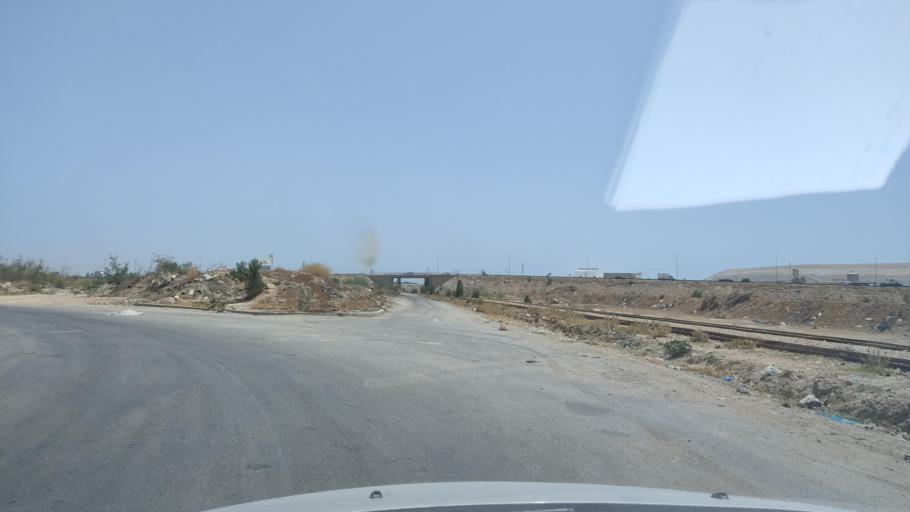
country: TN
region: Safaqis
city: Sfax
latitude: 34.7054
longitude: 10.7177
